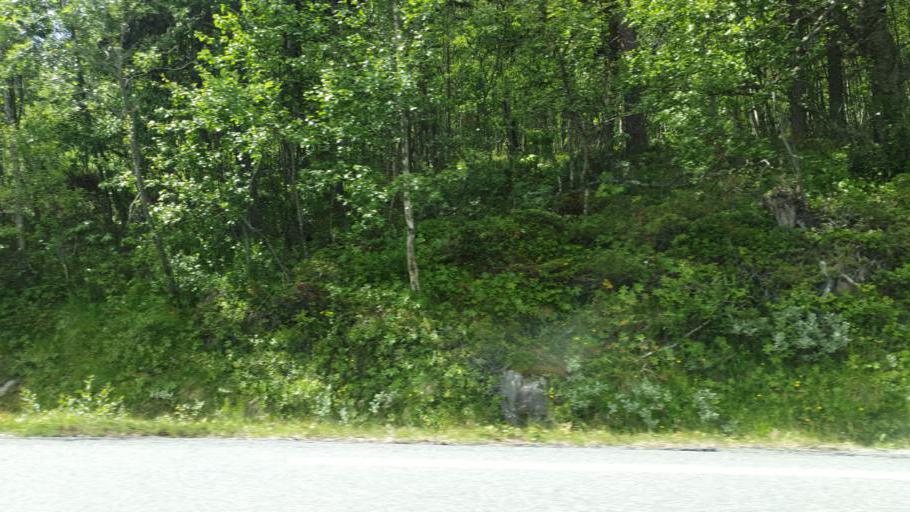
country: NO
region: Oppland
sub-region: Vaga
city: Vagamo
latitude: 61.7488
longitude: 9.0823
